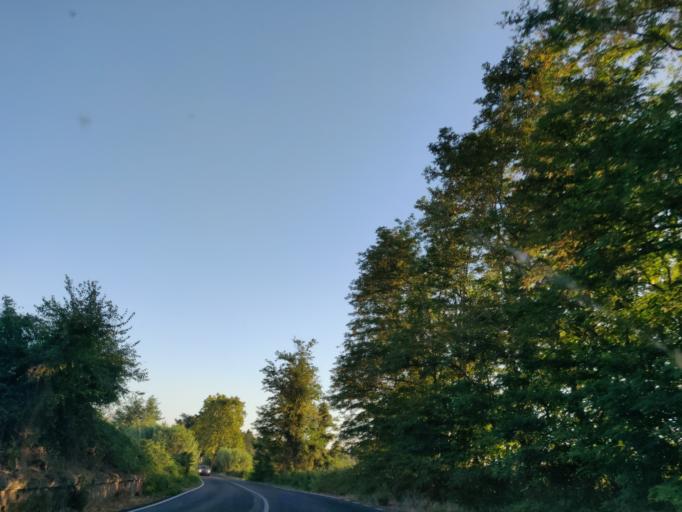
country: IT
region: Latium
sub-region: Provincia di Viterbo
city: Canino
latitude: 42.4078
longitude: 11.6957
